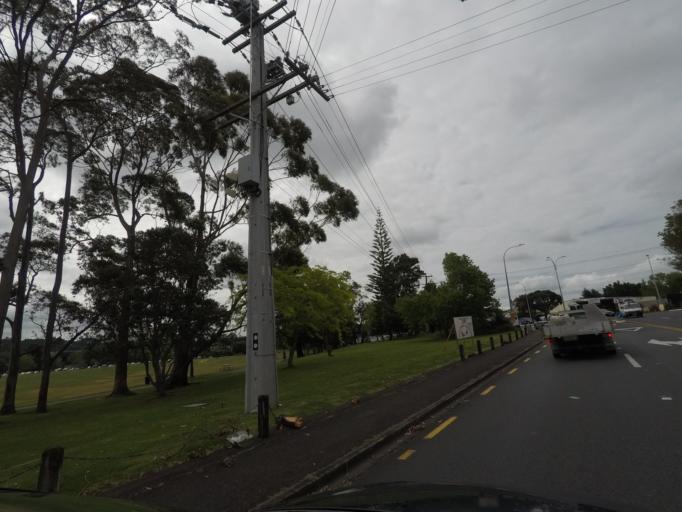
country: NZ
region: Auckland
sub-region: Auckland
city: Waitakere
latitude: -36.9075
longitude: 174.6278
